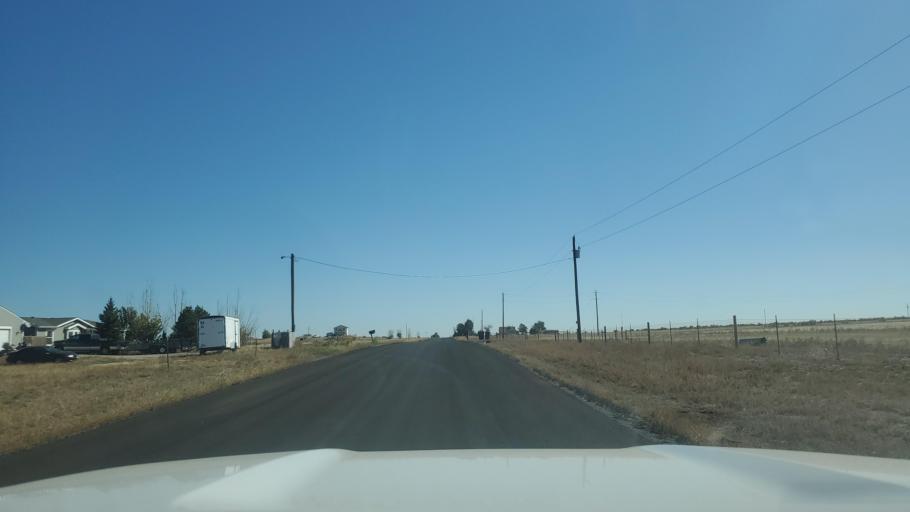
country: US
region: Colorado
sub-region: Adams County
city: Bennett
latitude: 39.7598
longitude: -104.3868
